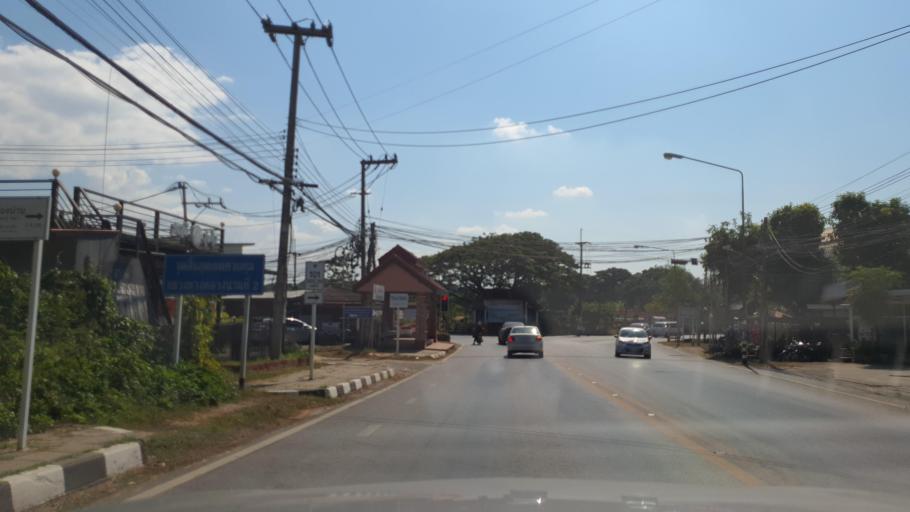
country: TH
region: Nan
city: Nan
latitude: 18.7925
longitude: 100.7800
